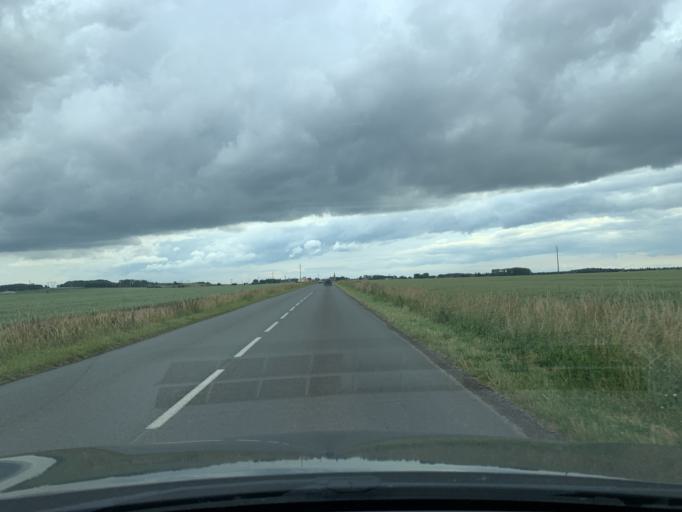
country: FR
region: Nord-Pas-de-Calais
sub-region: Departement du Nord
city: Cantin
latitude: 50.3243
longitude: 3.1458
